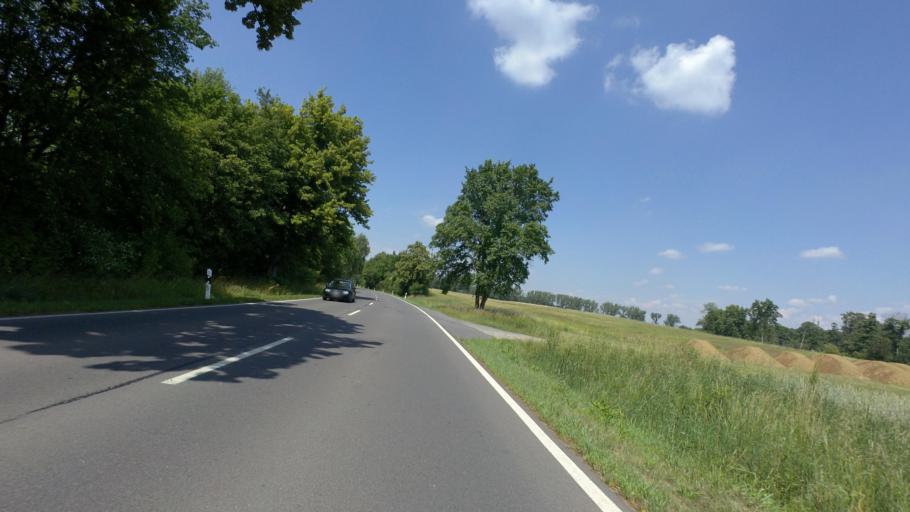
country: DE
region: Brandenburg
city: Angermunde
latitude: 52.9916
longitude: 14.0281
